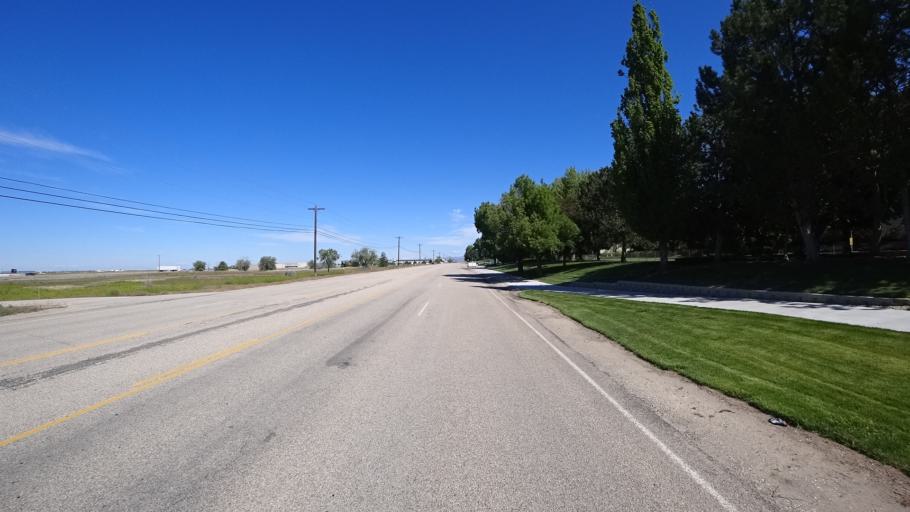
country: US
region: Idaho
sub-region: Ada County
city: Boise
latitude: 43.5275
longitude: -116.1496
